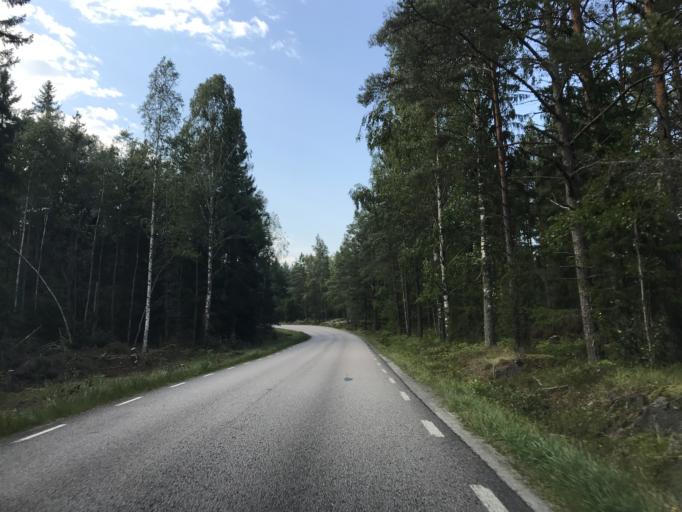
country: SE
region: Stockholm
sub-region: Norrtalje Kommun
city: Bjorko
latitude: 59.8804
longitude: 18.9825
